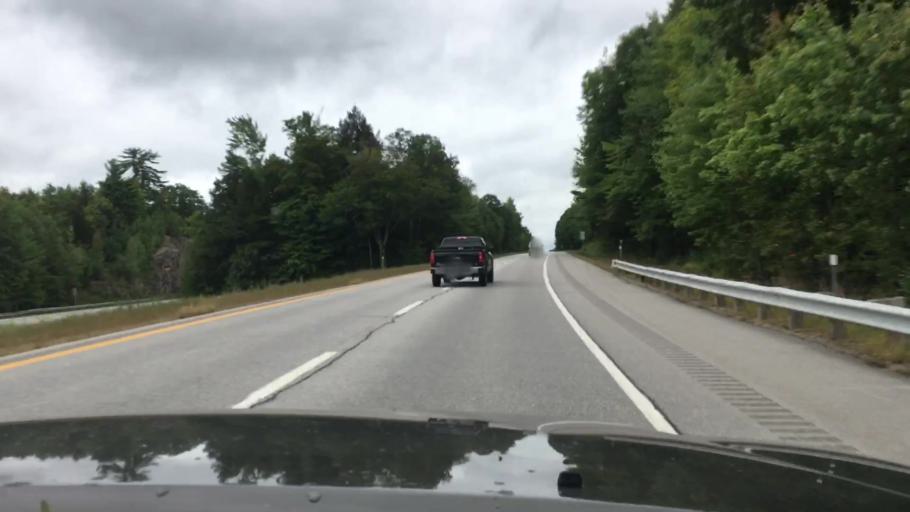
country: US
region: New Hampshire
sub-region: Belknap County
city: Sanbornton
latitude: 43.5608
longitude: -71.6177
